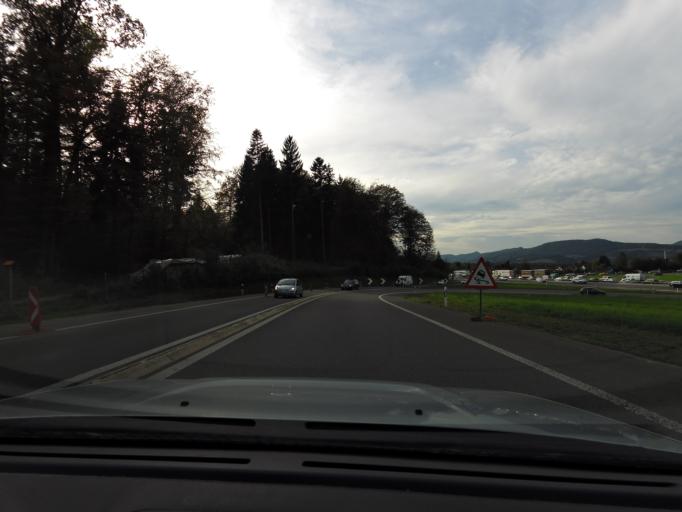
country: CH
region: Aargau
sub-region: Bezirk Lenzburg
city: Niederlenz
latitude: 47.3969
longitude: 8.1894
